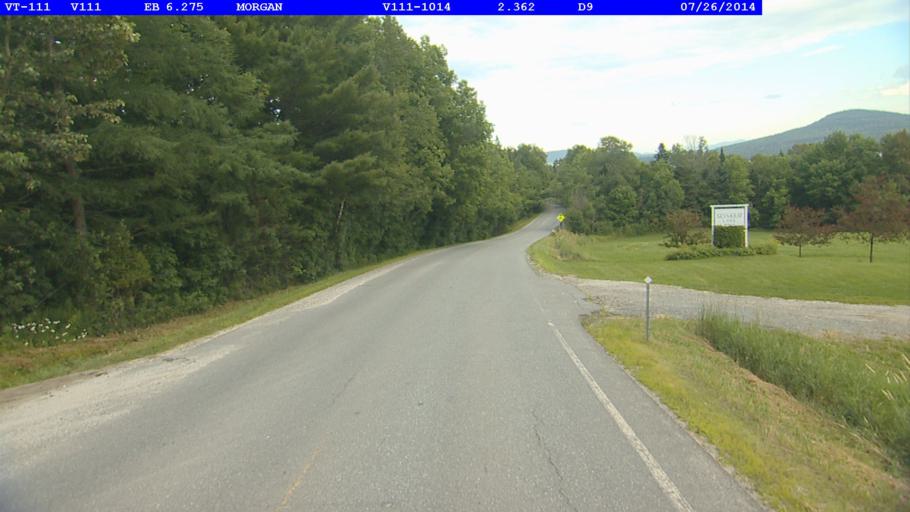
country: US
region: Vermont
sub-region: Orleans County
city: Newport
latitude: 44.9167
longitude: -72.0226
